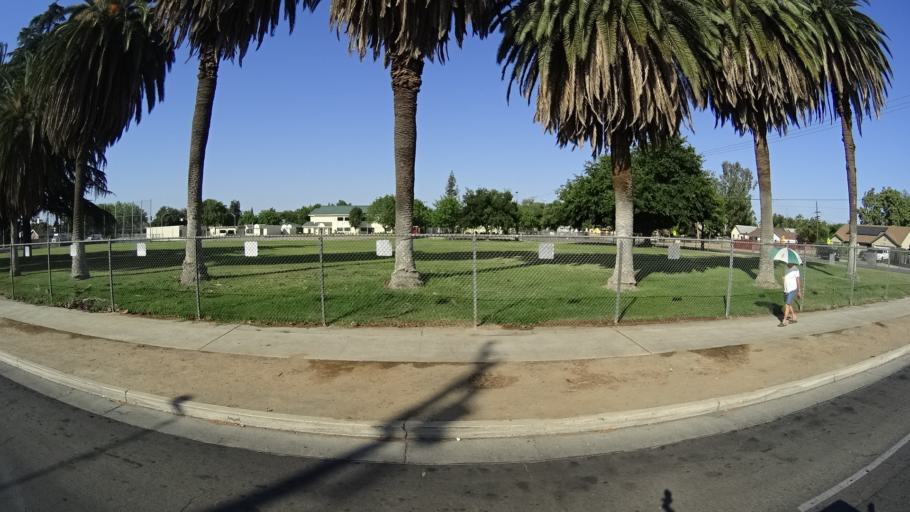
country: US
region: California
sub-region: Fresno County
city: Fresno
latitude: 36.7248
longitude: -119.7944
